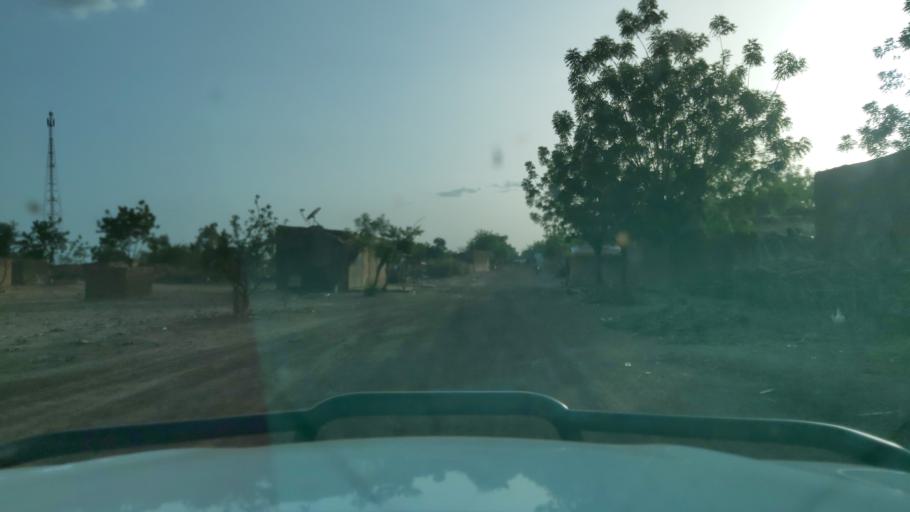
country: ML
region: Koulikoro
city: Kolokani
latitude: 13.2034
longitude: -7.9288
